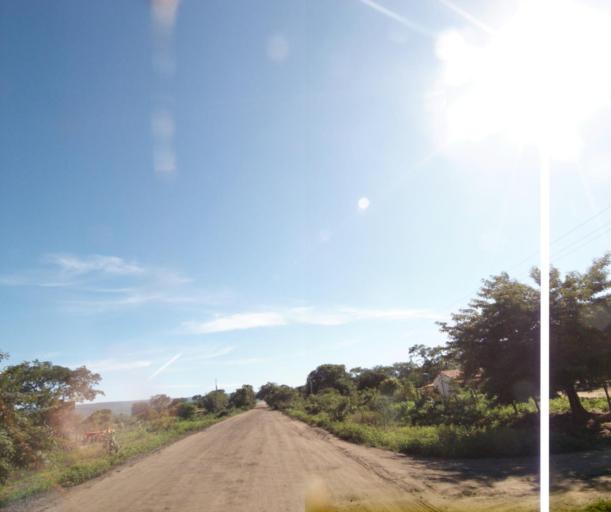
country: BR
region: Bahia
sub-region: Sao Felix Do Coribe
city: Santa Maria da Vitoria
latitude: -13.6292
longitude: -44.4250
